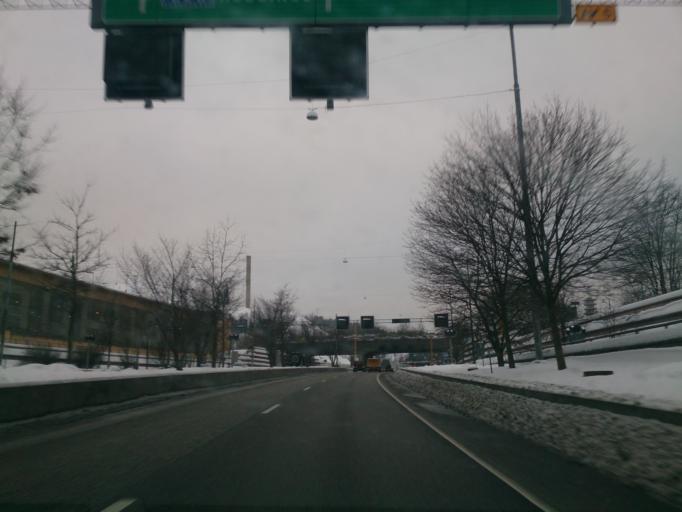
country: SE
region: Stockholm
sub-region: Stockholms Kommun
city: OEstermalm
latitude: 59.3035
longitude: 18.1137
